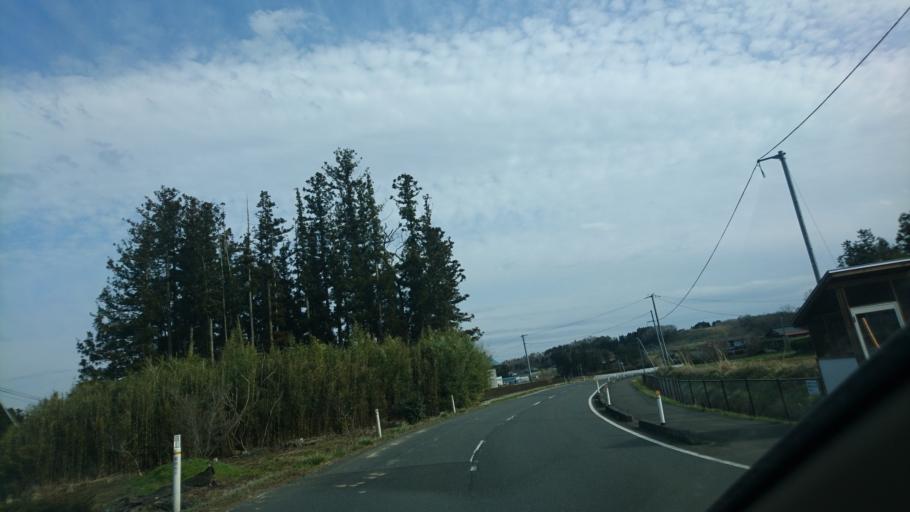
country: JP
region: Iwate
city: Ichinoseki
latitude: 38.8102
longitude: 141.0304
